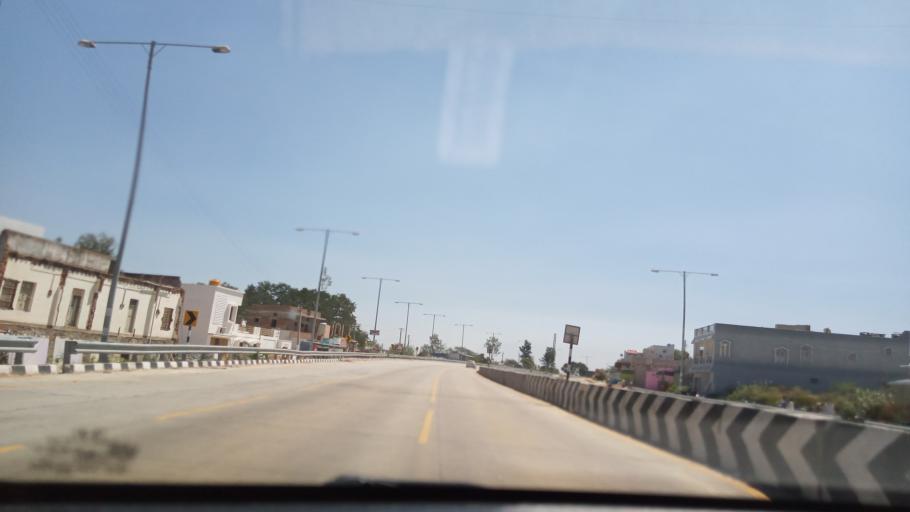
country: IN
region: Andhra Pradesh
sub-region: Chittoor
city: Palmaner
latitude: 13.1831
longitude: 78.6398
